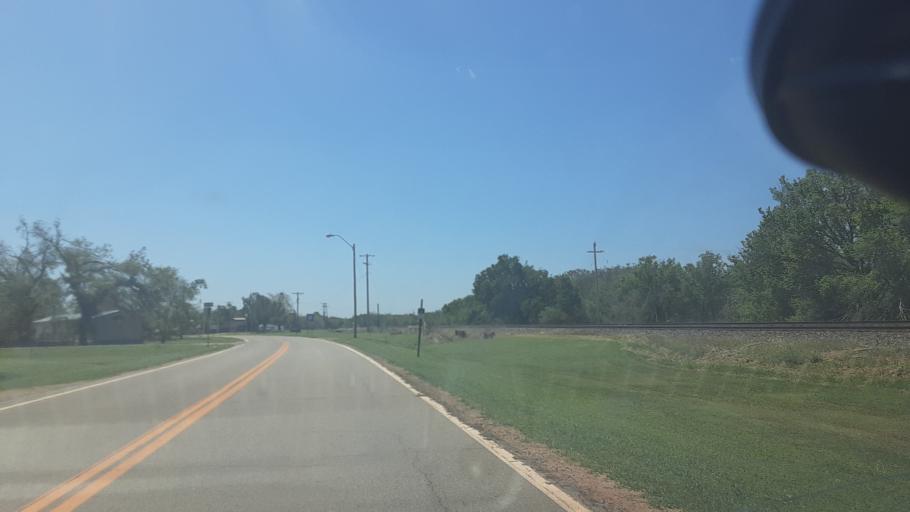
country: US
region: Oklahoma
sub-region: Logan County
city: Guthrie
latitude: 36.0688
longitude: -97.4067
